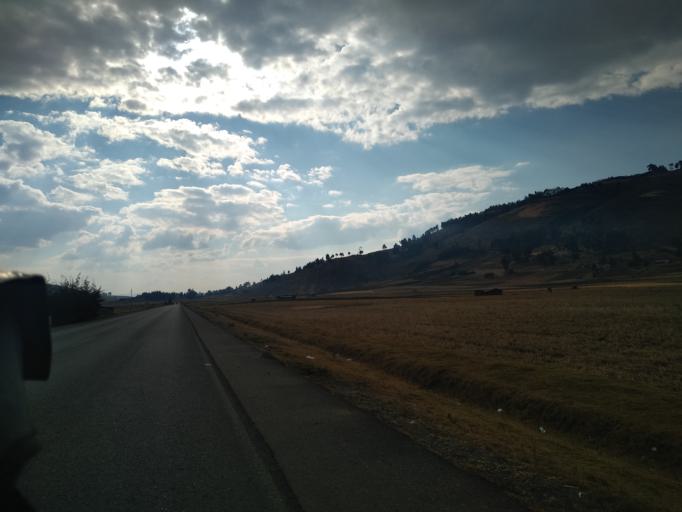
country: PE
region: Cajamarca
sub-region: Provincia de Cajamarca
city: Encanada
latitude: -7.1396
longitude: -78.3770
